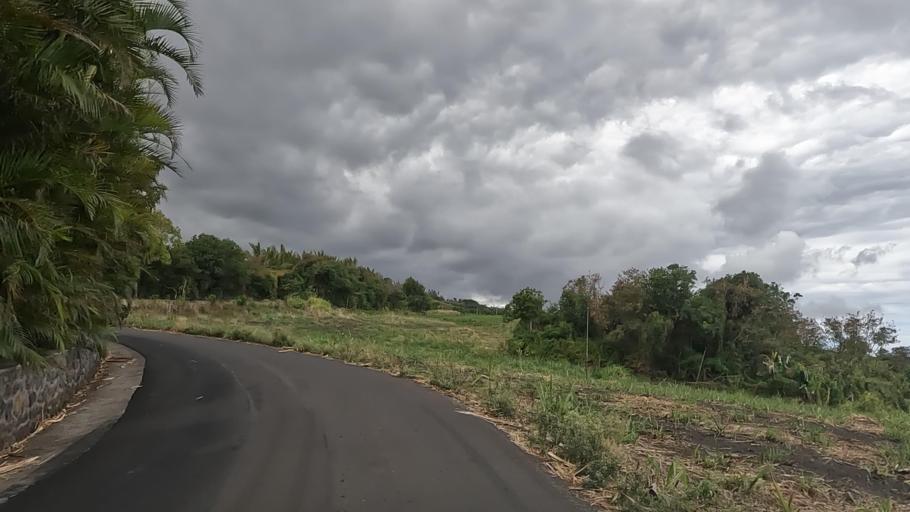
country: RE
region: Reunion
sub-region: Reunion
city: Saint-Pierre
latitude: -21.3409
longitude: 55.5219
